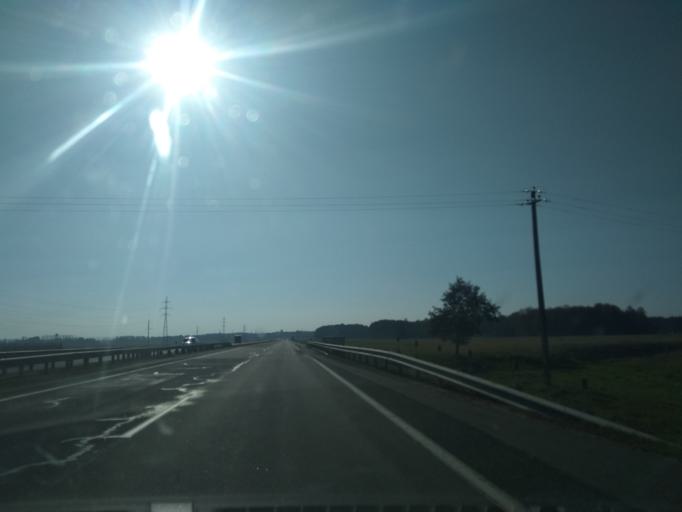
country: BY
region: Brest
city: Horad Kobryn
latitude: 52.1998
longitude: 24.4159
